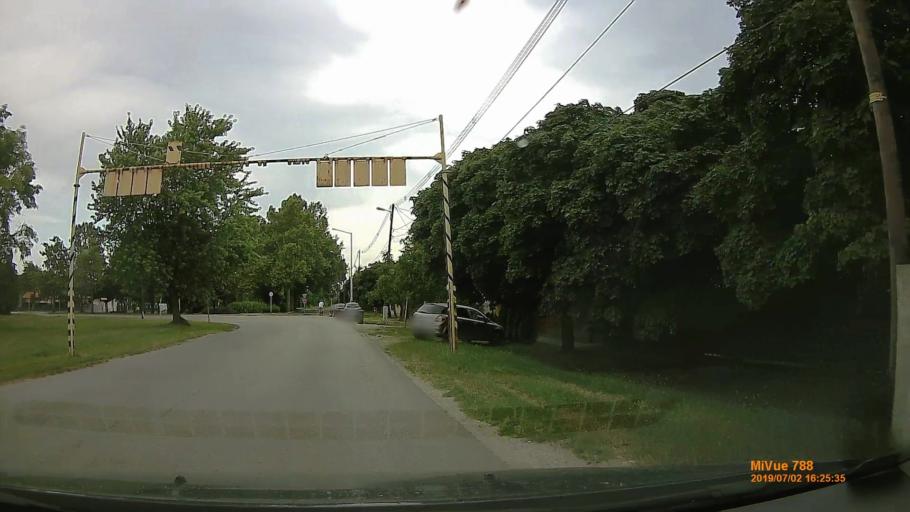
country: HU
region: Gyor-Moson-Sopron
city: Mosonmagyarovar
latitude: 47.8667
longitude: 17.2587
